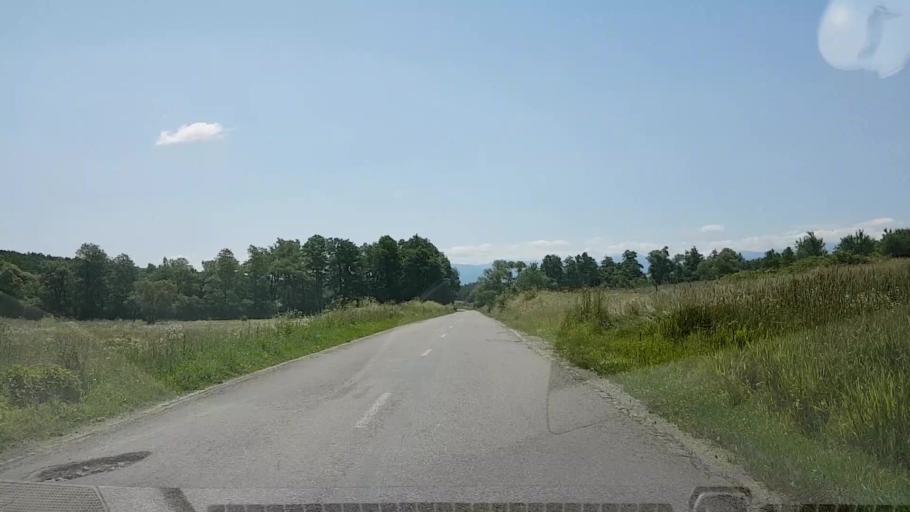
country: RO
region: Brasov
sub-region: Comuna Cincu
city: Cincu
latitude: 45.8810
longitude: 24.8139
